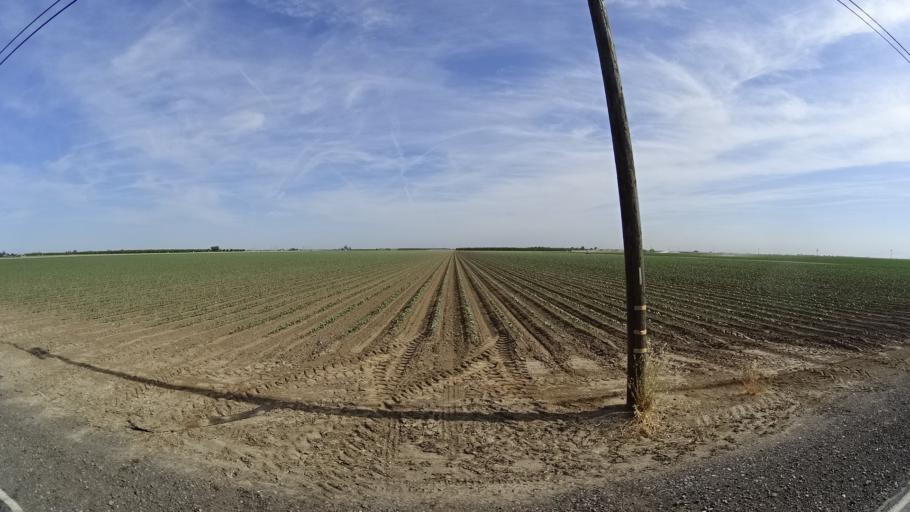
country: US
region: California
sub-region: Kings County
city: Home Garden
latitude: 36.3428
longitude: -119.5515
